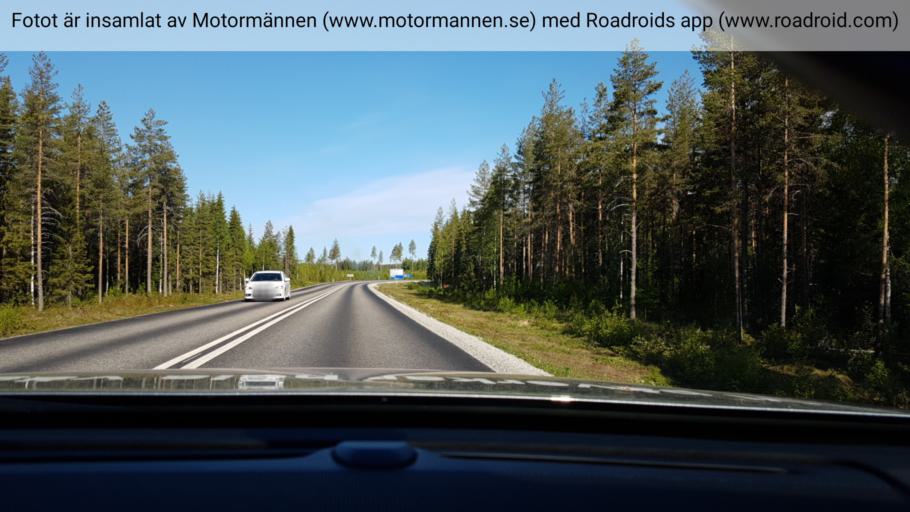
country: SE
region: Vaesterbotten
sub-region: Vindelns Kommun
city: Vindeln
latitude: 64.0542
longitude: 19.6574
